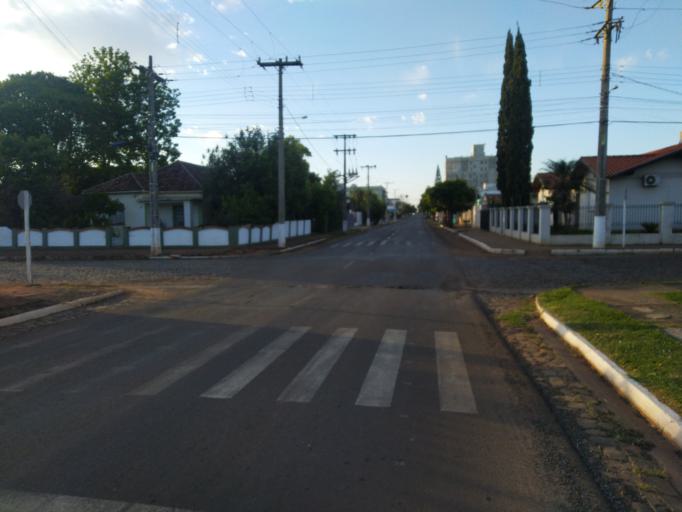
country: BR
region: Rio Grande do Sul
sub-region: Sao Borja
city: Sao Borja
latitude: -28.6528
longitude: -56.0106
